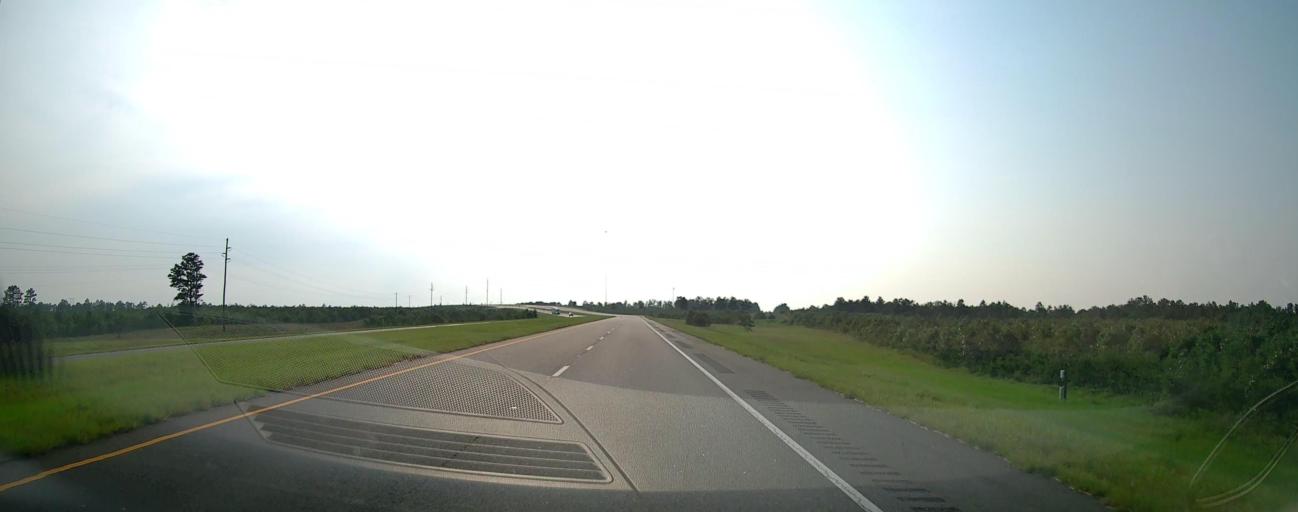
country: US
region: Georgia
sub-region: Talbot County
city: Talbotton
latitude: 32.5963
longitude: -84.4434
